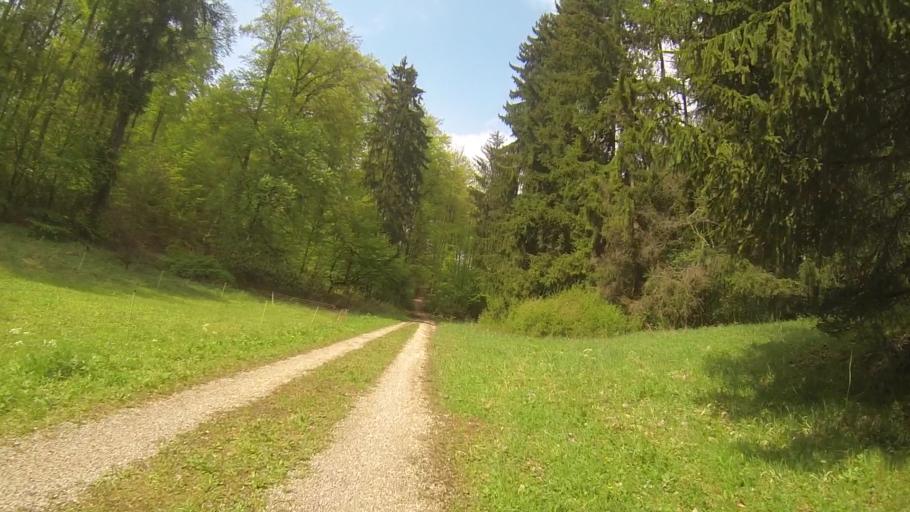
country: DE
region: Baden-Wuerttemberg
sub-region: Regierungsbezirk Stuttgart
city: Nattheim
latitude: 48.6689
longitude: 10.2216
